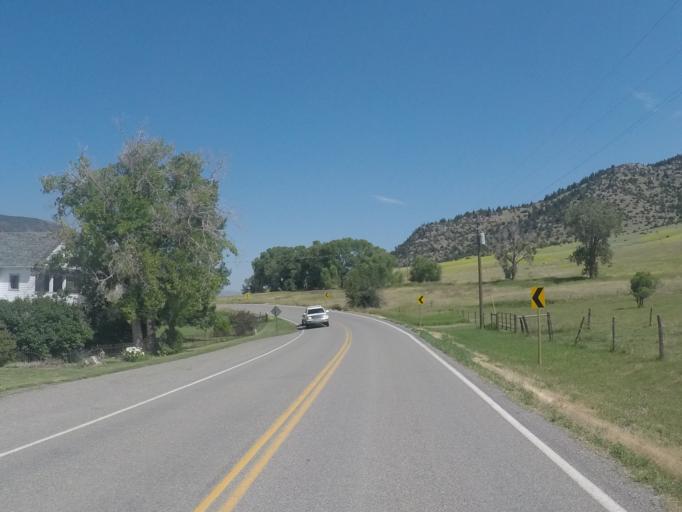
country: US
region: Montana
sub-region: Park County
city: Livingston
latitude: 45.5679
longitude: -110.5587
